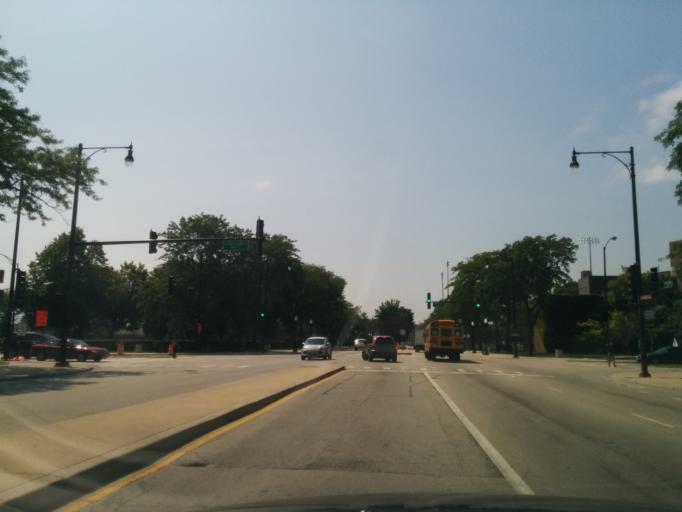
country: US
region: Illinois
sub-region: Cook County
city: Chicago
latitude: 41.8696
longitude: -87.6472
